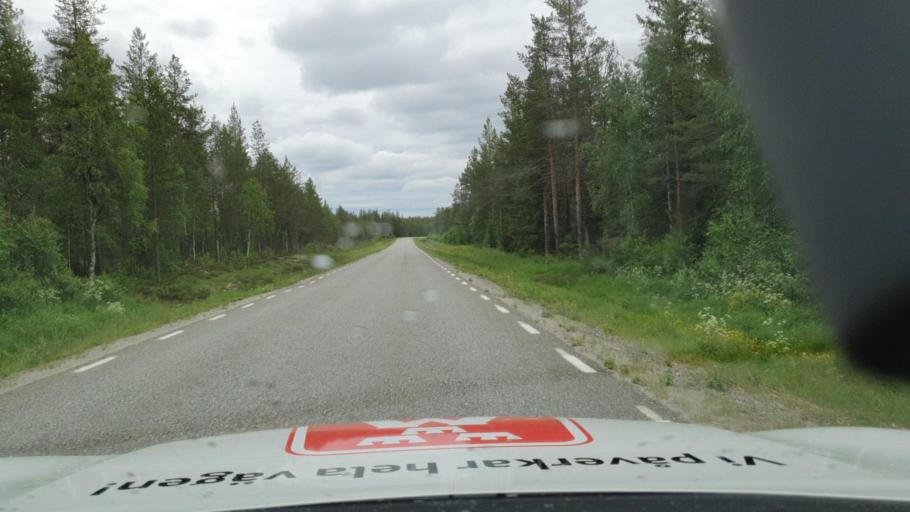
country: SE
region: Vaesterbotten
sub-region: Lycksele Kommun
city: Lycksele
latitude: 64.2605
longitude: 18.2088
